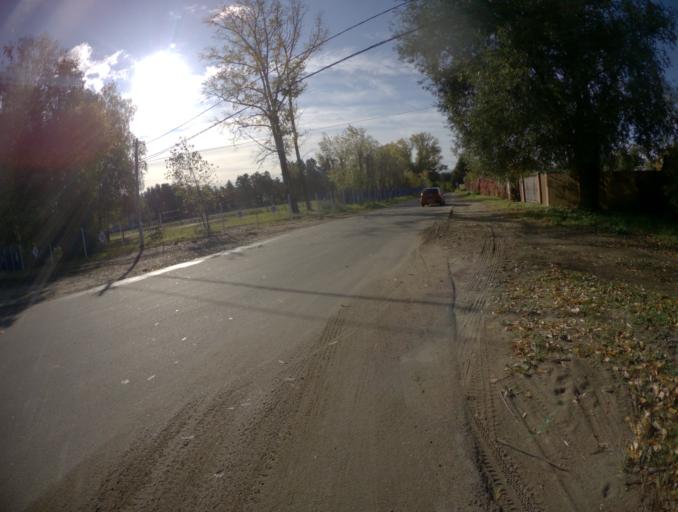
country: RU
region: Vladimir
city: Petushki
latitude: 55.9173
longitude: 39.4634
